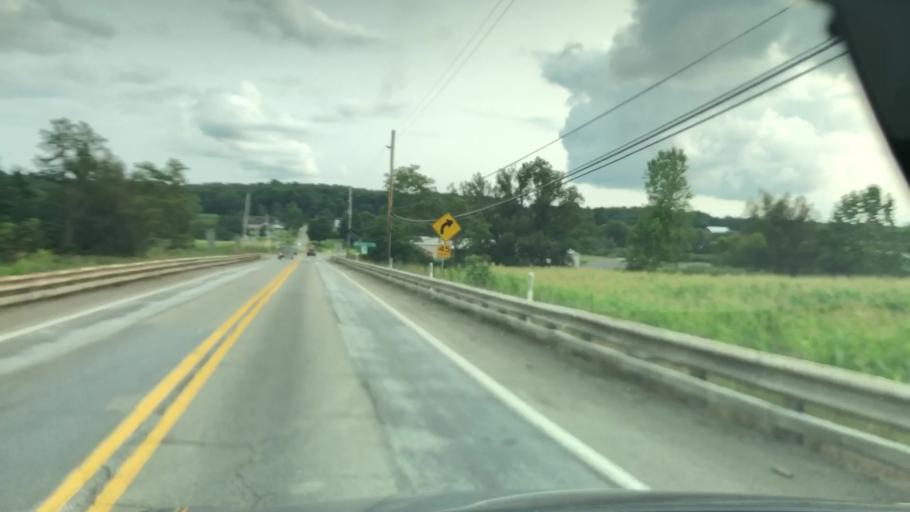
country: US
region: Pennsylvania
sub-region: Erie County
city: Union City
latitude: 41.9975
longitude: -79.8109
